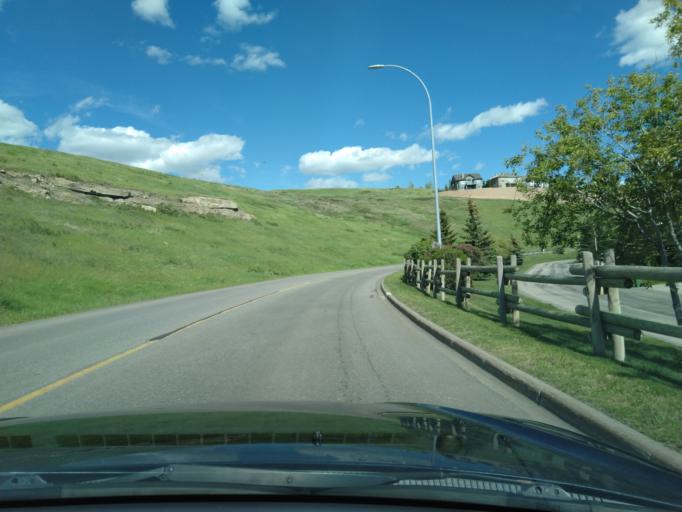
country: CA
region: Alberta
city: Cochrane
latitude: 51.1947
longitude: -114.4356
